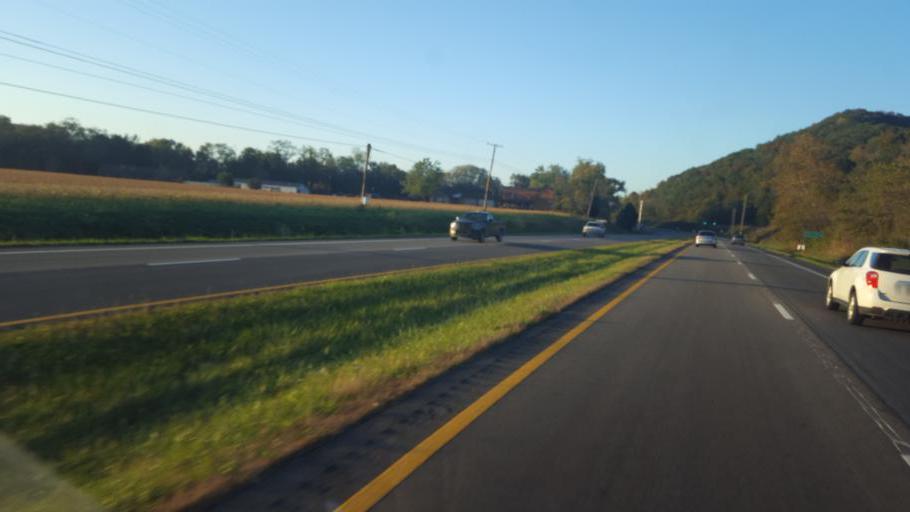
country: US
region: Ohio
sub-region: Scioto County
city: Lucasville
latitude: 38.8386
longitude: -82.9842
